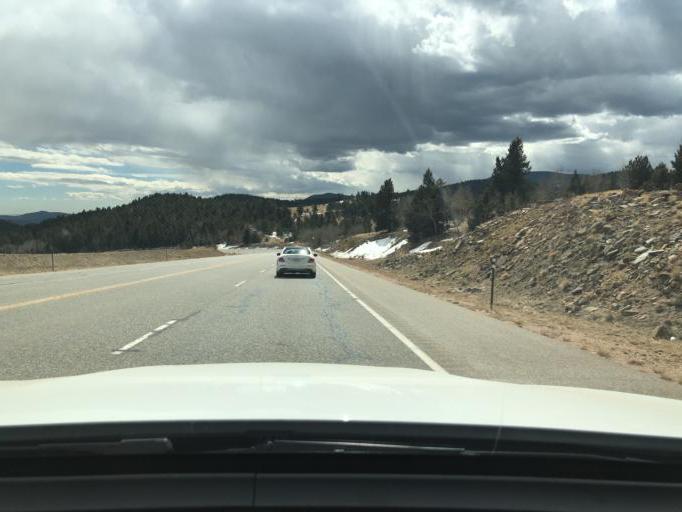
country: US
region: Colorado
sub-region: Gilpin County
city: Central City
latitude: 39.7875
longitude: -105.4970
